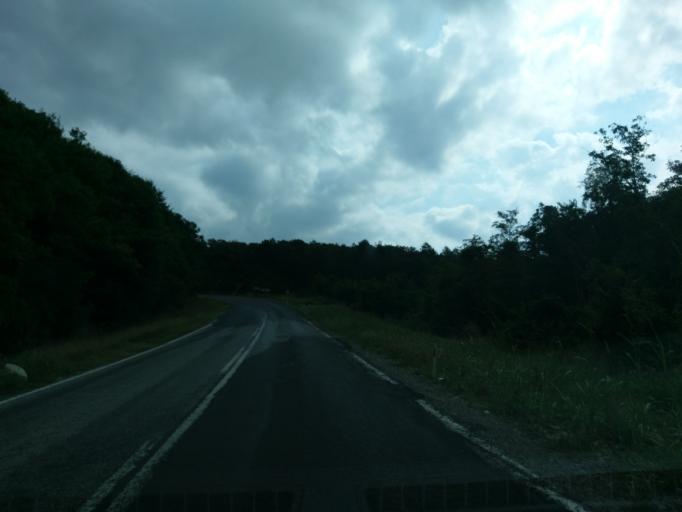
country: TR
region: Sinop
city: Yenikonak
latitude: 41.9432
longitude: 34.7327
